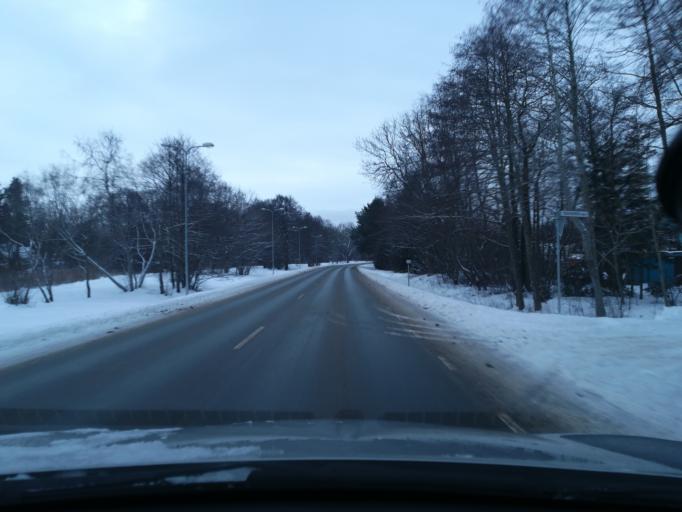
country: EE
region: Harju
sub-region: Keila linn
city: Keila
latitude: 59.4392
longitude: 24.3713
